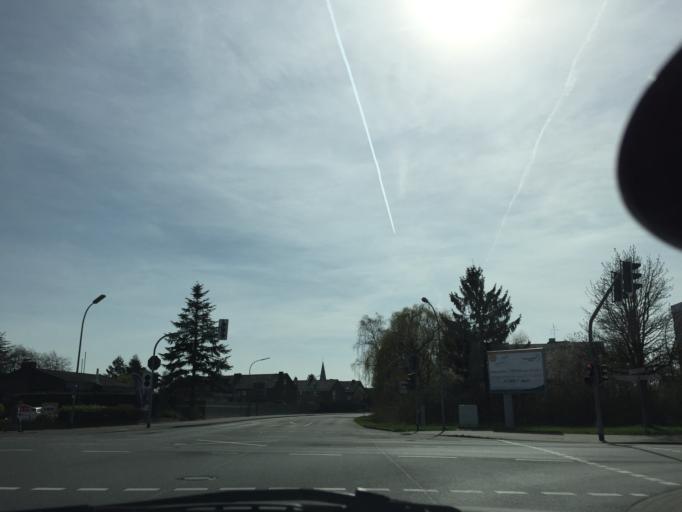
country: DE
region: North Rhine-Westphalia
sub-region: Regierungsbezirk Dusseldorf
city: Goch
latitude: 51.6807
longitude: 6.1447
